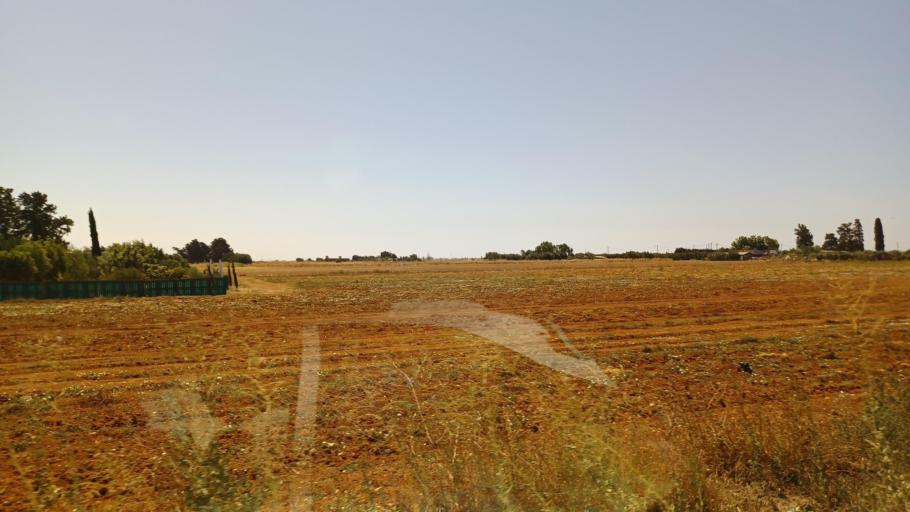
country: CY
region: Larnaka
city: Xylotymbou
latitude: 35.0285
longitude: 33.7306
